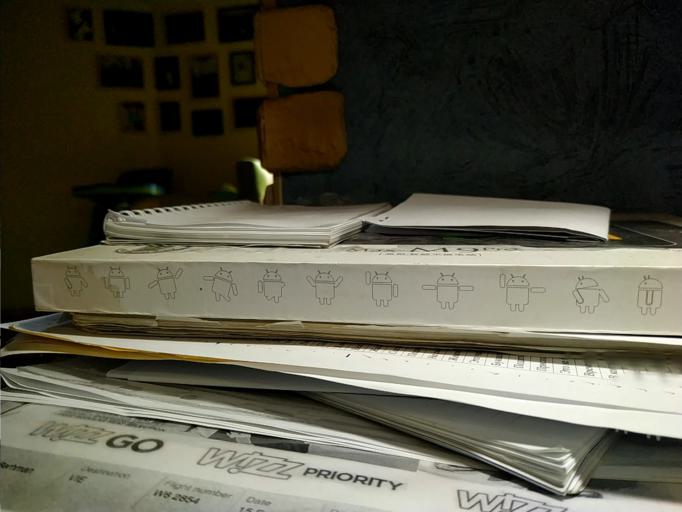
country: RU
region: Novgorod
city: Poddor'ye
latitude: 57.5213
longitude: 30.9164
